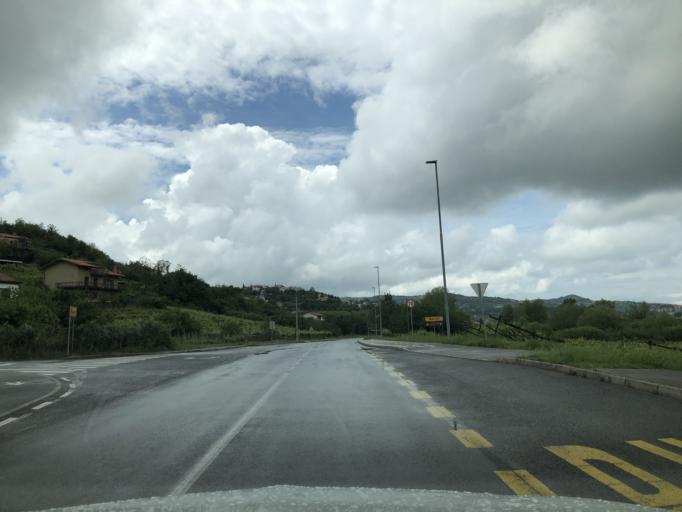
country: SI
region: Koper-Capodistria
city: Prade
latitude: 45.5177
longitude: 13.7614
